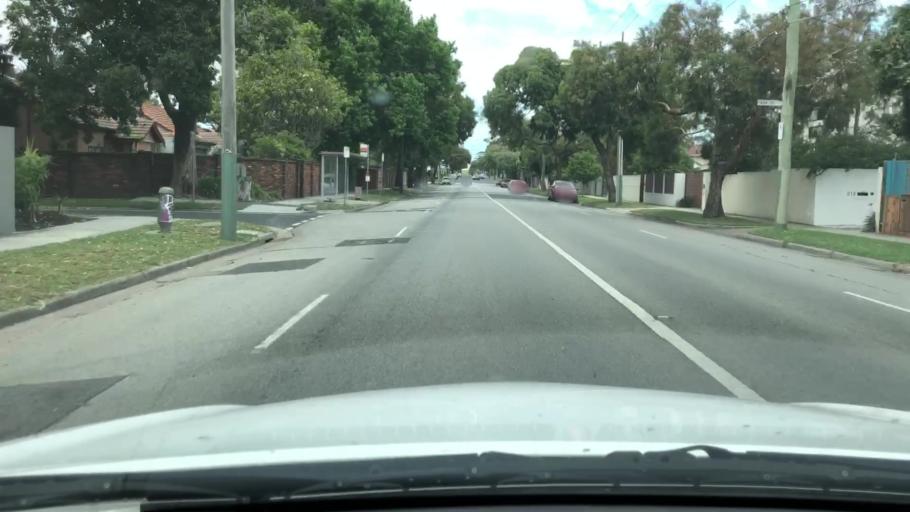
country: AU
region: Victoria
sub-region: Bayside
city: Black Rock
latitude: -37.9573
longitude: 145.0199
